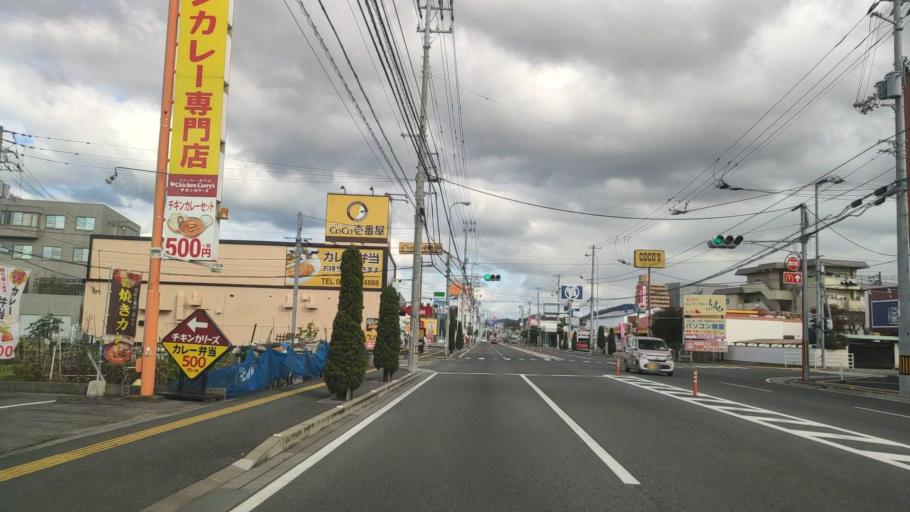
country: JP
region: Ehime
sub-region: Shikoku-chuo Shi
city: Matsuyama
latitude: 33.8586
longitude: 132.7488
